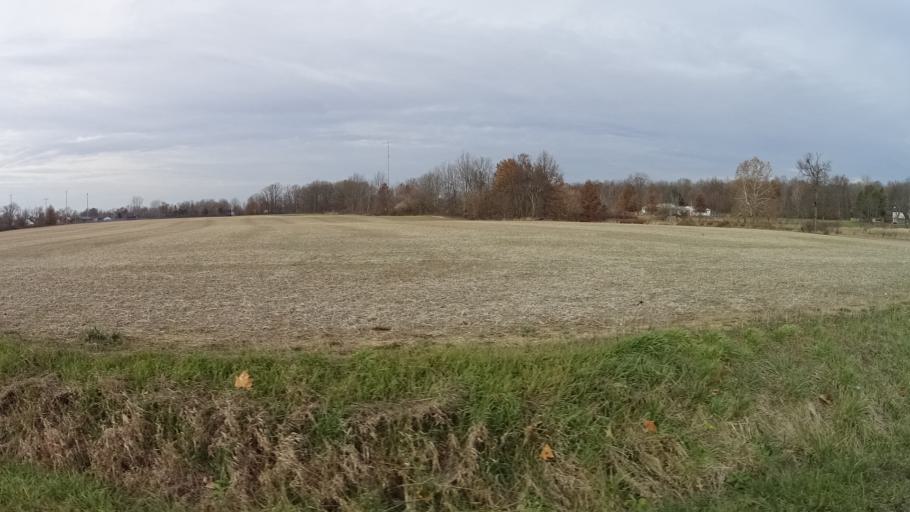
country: US
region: Ohio
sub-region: Lorain County
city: Lagrange
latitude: 41.1716
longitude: -82.1106
